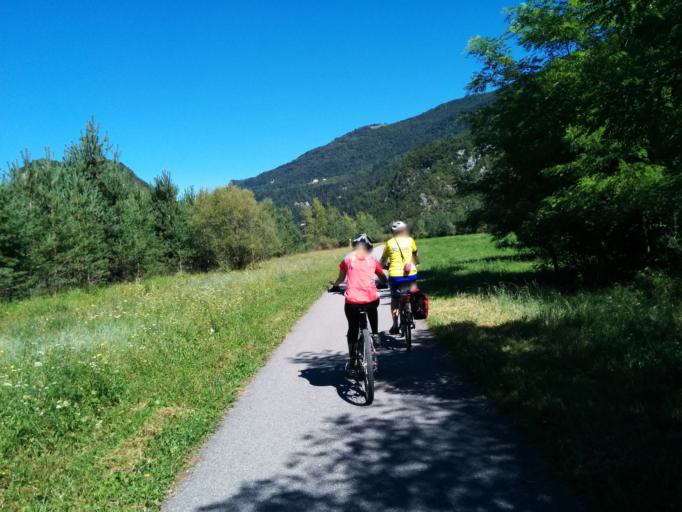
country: IT
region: Friuli Venezia Giulia
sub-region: Provincia di Udine
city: Villa Santina
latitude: 46.4155
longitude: 12.9076
